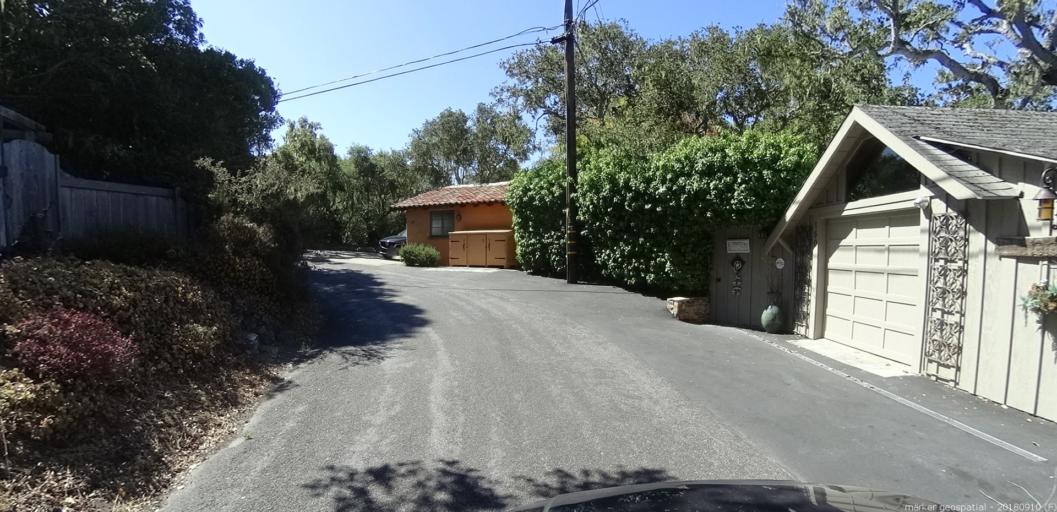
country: US
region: California
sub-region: Monterey County
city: Carmel-by-the-Sea
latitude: 36.5005
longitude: -121.9346
